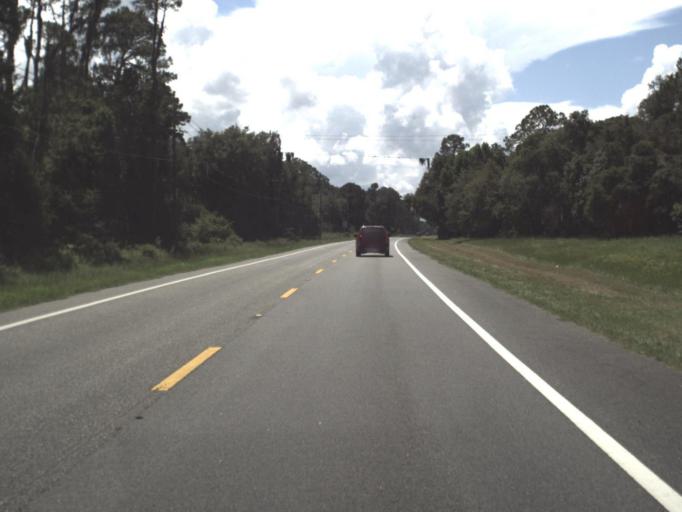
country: US
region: Florida
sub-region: Putnam County
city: Crescent City
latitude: 29.4704
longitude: -81.5307
